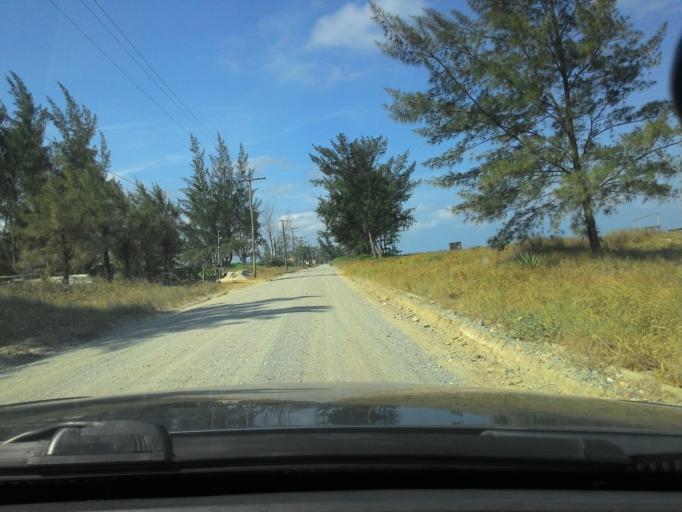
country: BR
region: Sao Paulo
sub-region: Iguape
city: Iguape
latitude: -24.8407
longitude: -47.6816
